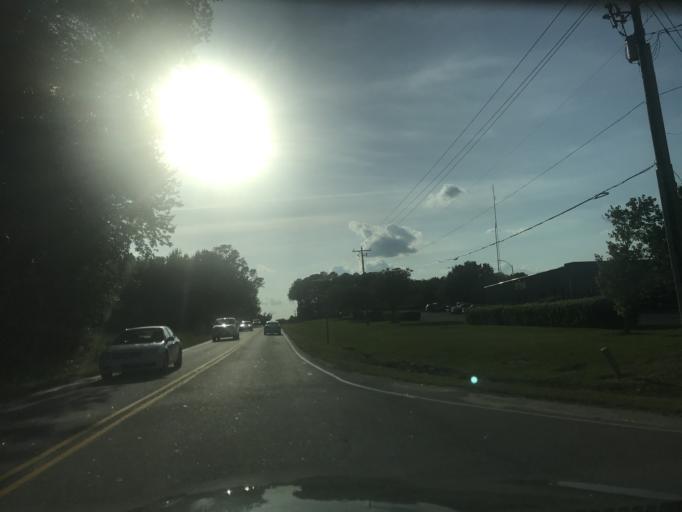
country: US
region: North Carolina
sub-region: Wake County
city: Knightdale
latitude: 35.7521
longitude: -78.4955
